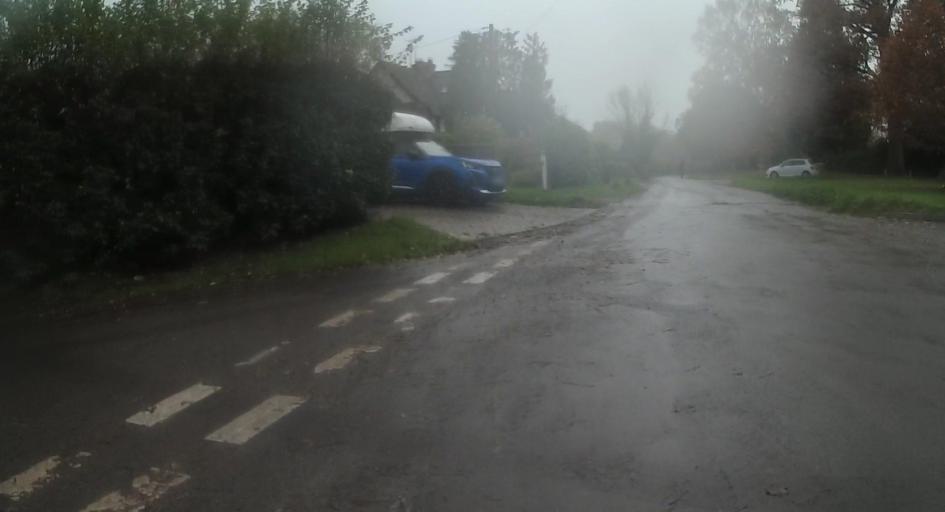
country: GB
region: England
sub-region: Wokingham
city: Finchampstead
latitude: 51.3686
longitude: -0.8617
